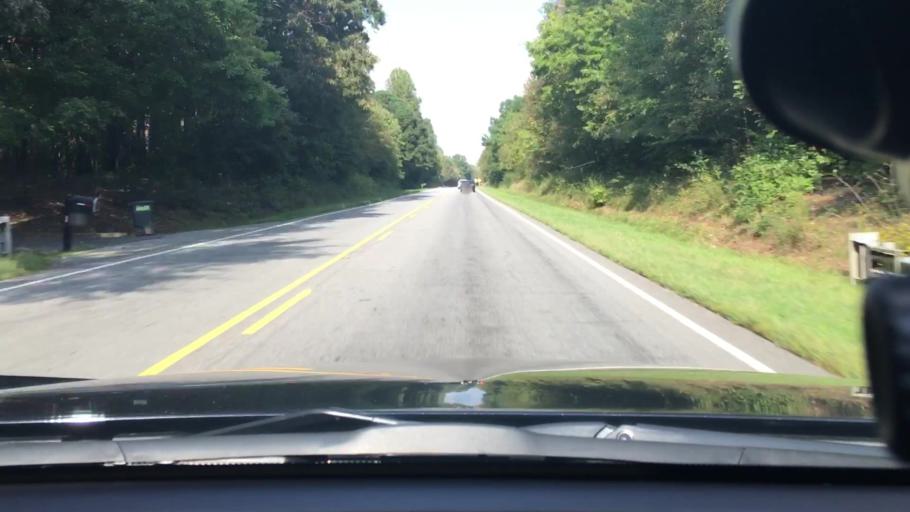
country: US
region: North Carolina
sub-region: Randolph County
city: Asheboro
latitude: 35.6694
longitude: -79.8778
